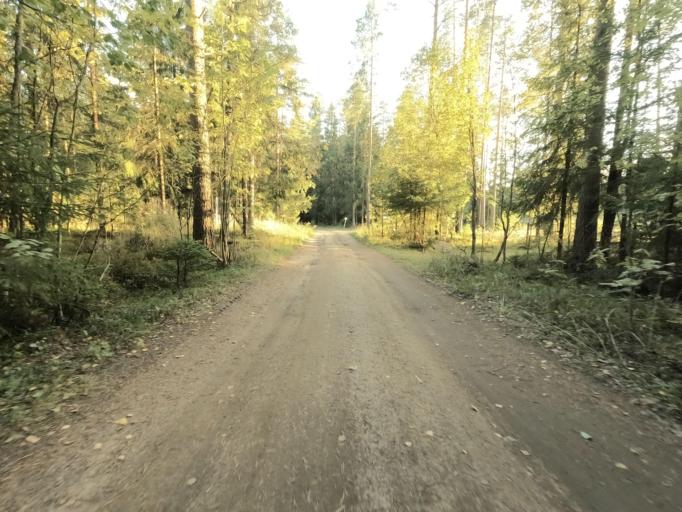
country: RU
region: Leningrad
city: Otradnoye
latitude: 59.8239
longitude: 30.7724
